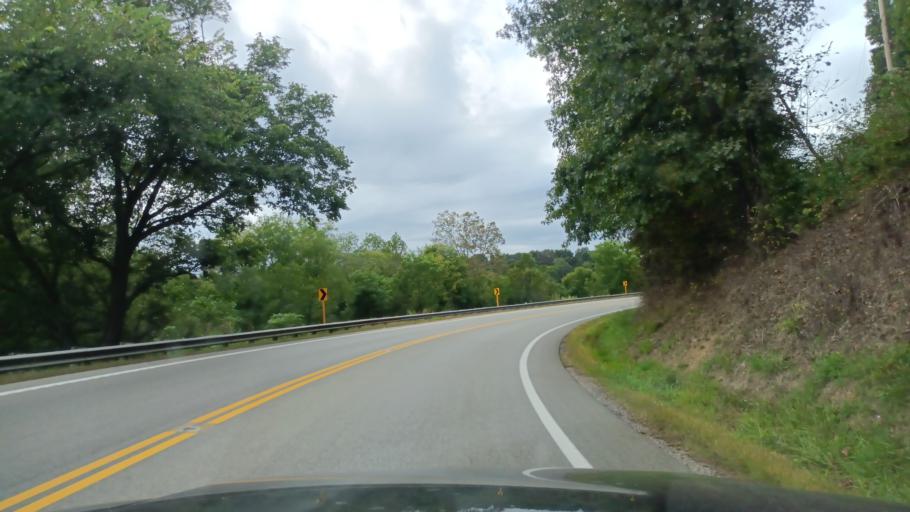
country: US
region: Ohio
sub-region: Vinton County
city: McArthur
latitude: 39.2699
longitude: -82.6520
